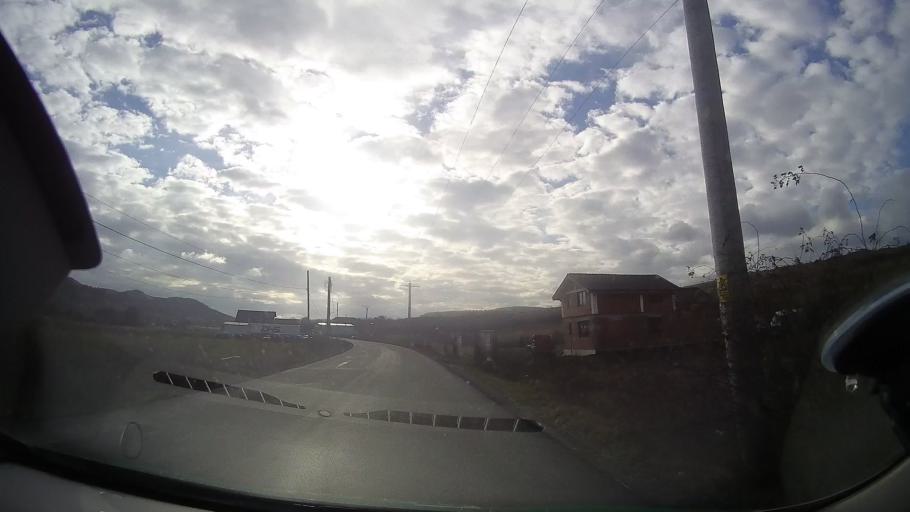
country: RO
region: Cluj
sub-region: Comuna Floresti
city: Luna de Sus
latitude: 46.7220
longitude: 23.4220
